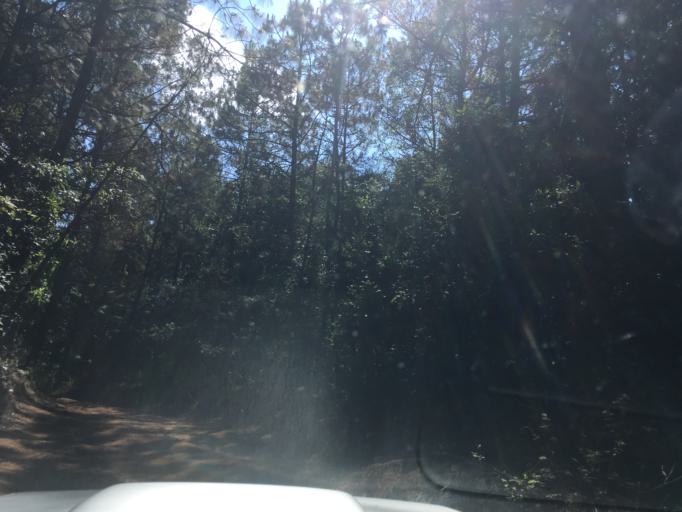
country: MX
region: Michoacan
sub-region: Zitacuaro
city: La Fundicion (Quinta Manzana)
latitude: 19.4976
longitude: -100.3088
